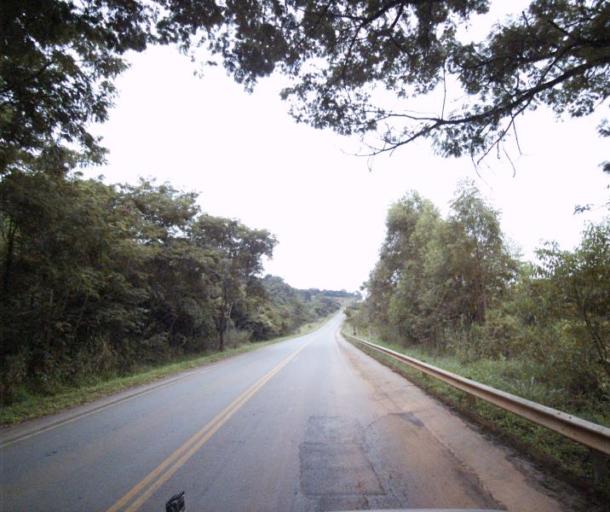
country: BR
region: Goias
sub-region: Pirenopolis
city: Pirenopolis
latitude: -15.9607
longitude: -48.8169
